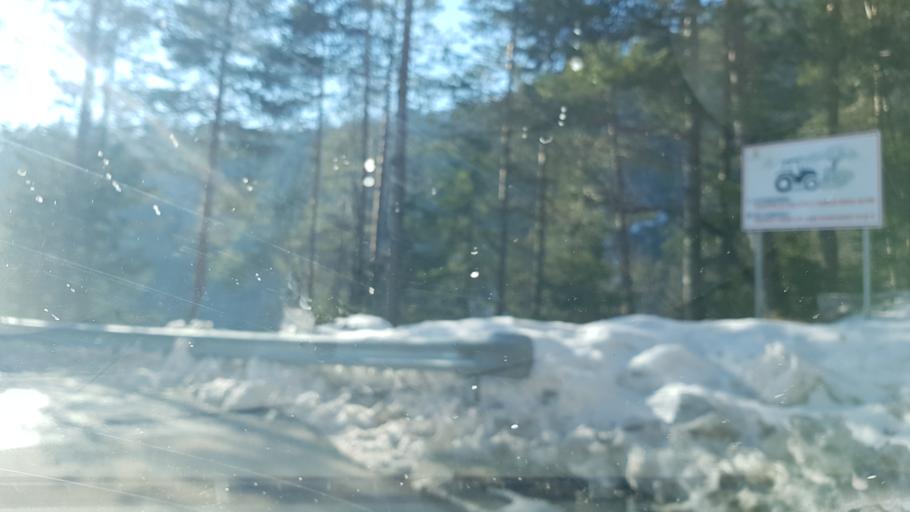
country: IT
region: Friuli Venezia Giulia
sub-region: Provincia di Udine
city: Malborghetto
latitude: 46.5178
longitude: 13.4702
